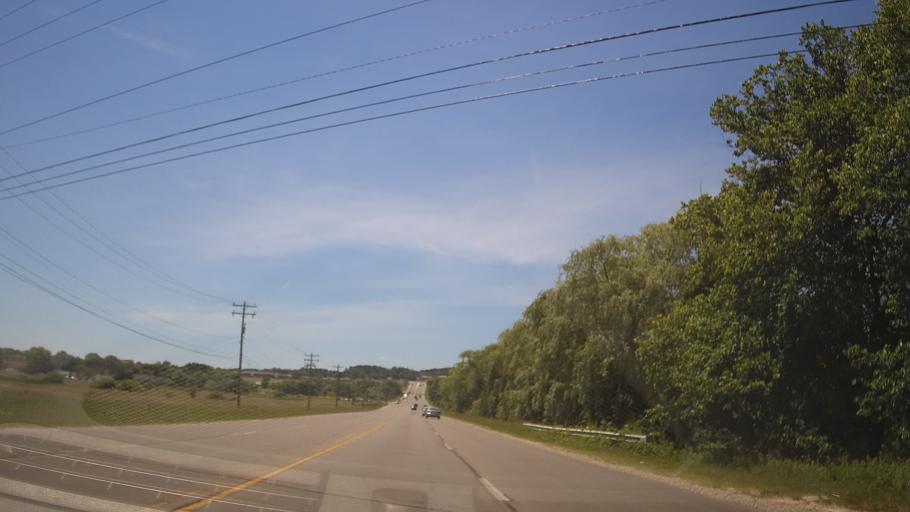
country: US
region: Michigan
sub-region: Grand Traverse County
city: Traverse City
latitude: 44.7497
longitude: -85.6400
